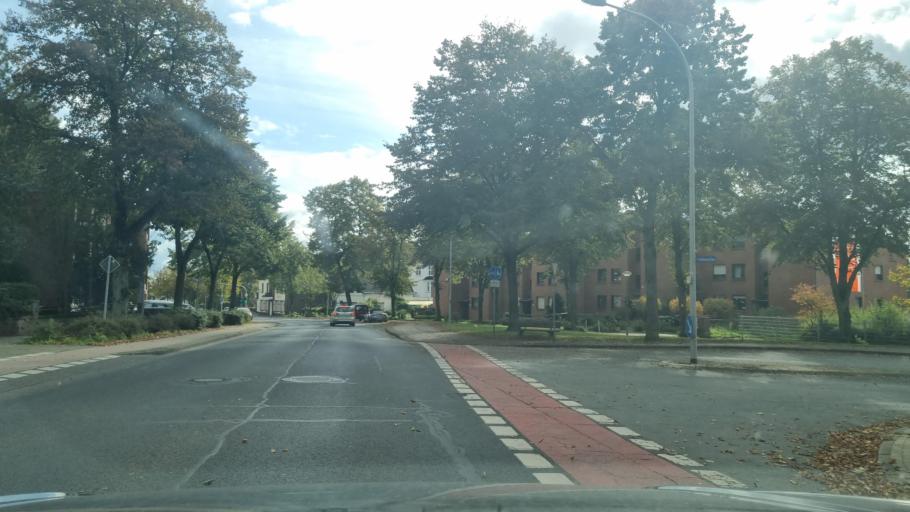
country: DE
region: North Rhine-Westphalia
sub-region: Regierungsbezirk Dusseldorf
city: Kleve
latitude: 51.7864
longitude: 6.1236
